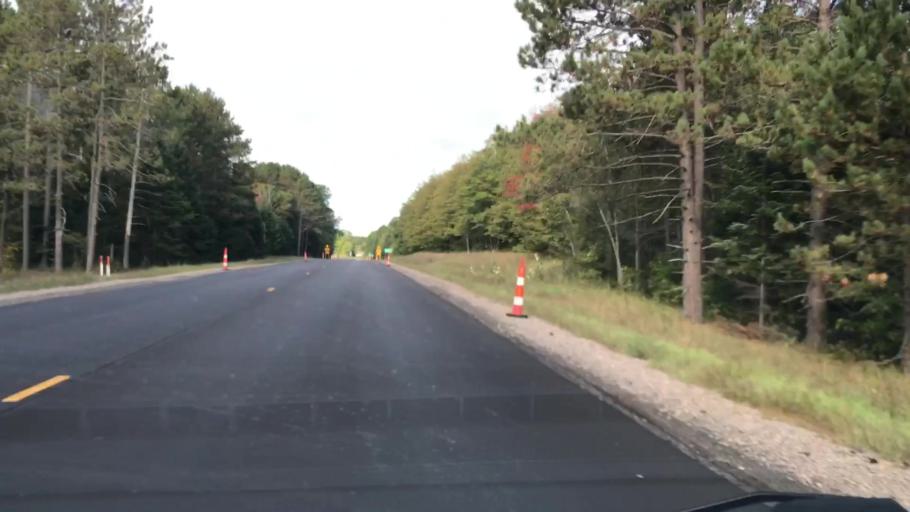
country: US
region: Michigan
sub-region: Luce County
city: Newberry
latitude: 46.3465
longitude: -85.0182
